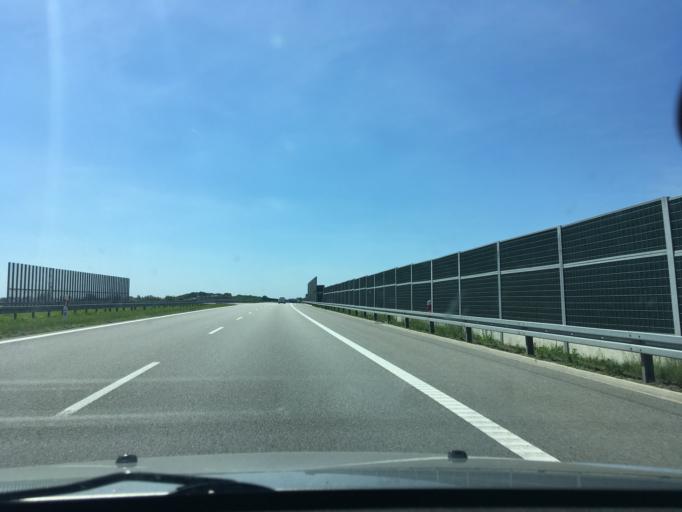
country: PL
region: Subcarpathian Voivodeship
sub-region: Powiat debicki
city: Zyrakow
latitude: 50.0816
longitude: 21.4070
